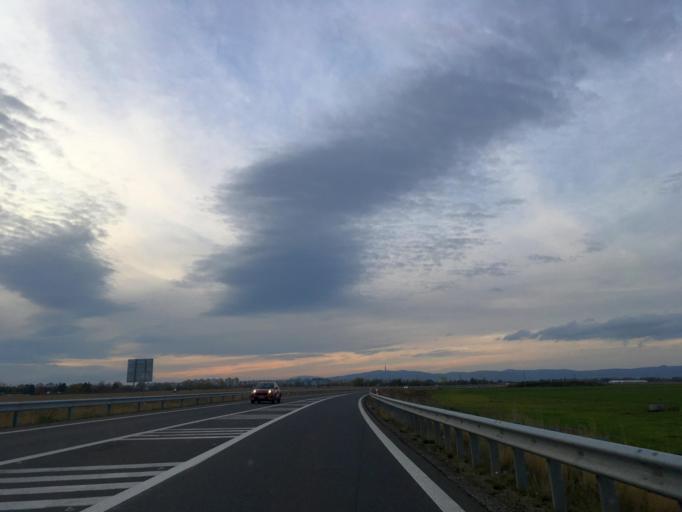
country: SK
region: Bratislavsky
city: Dunajska Luzna
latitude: 48.1325
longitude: 17.2433
